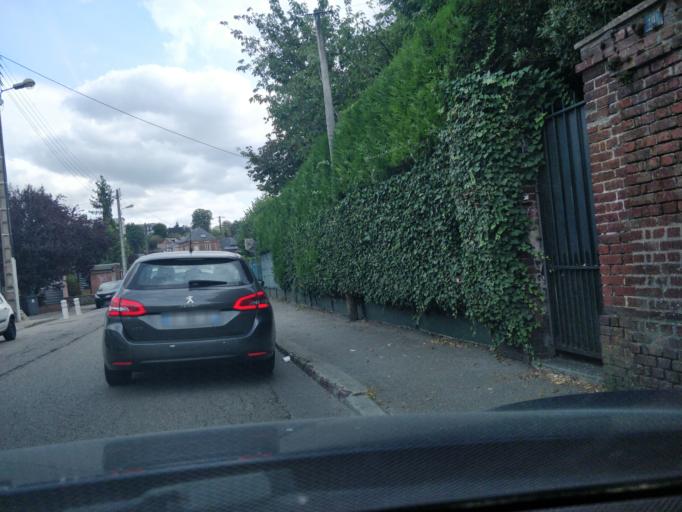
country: FR
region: Haute-Normandie
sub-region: Departement de la Seine-Maritime
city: Mont-Saint-Aignan
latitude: 49.4577
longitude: 1.0944
